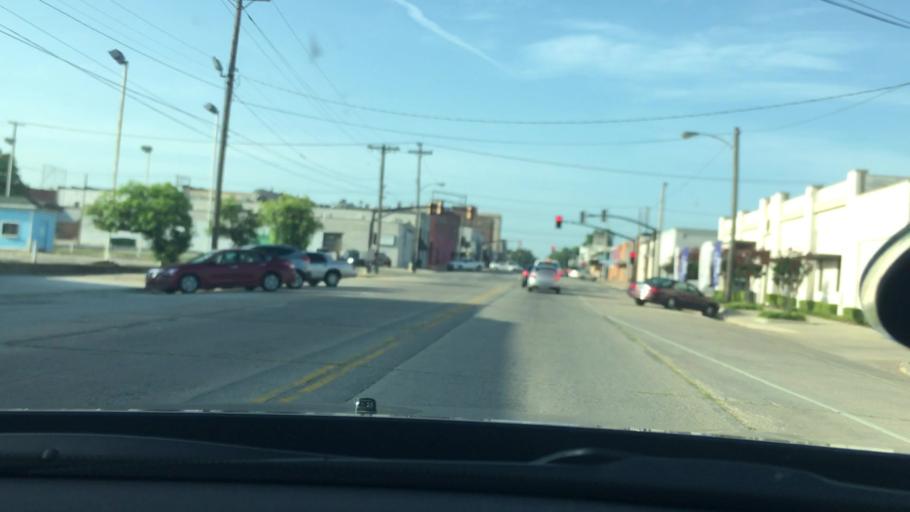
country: US
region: Oklahoma
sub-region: Pontotoc County
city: Ada
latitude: 34.7763
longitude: -96.6787
